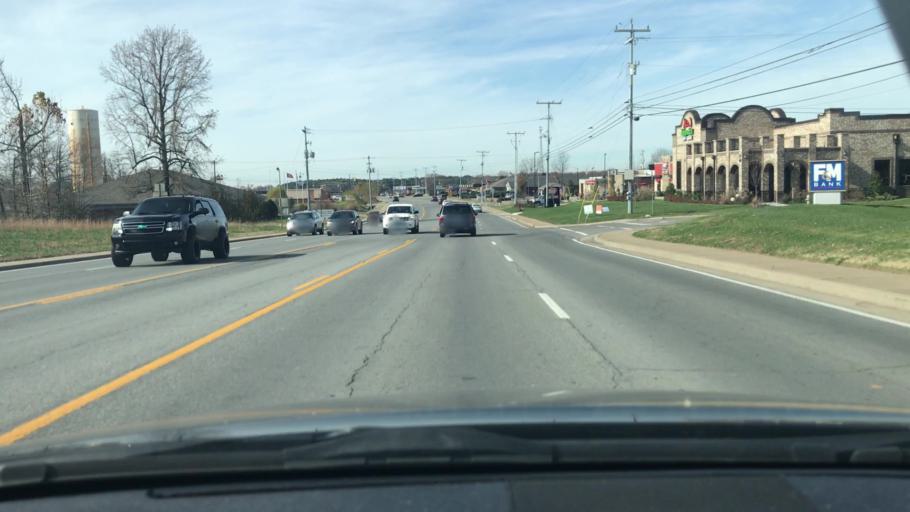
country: US
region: Tennessee
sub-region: Sumner County
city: White House
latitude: 36.4691
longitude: -86.6680
